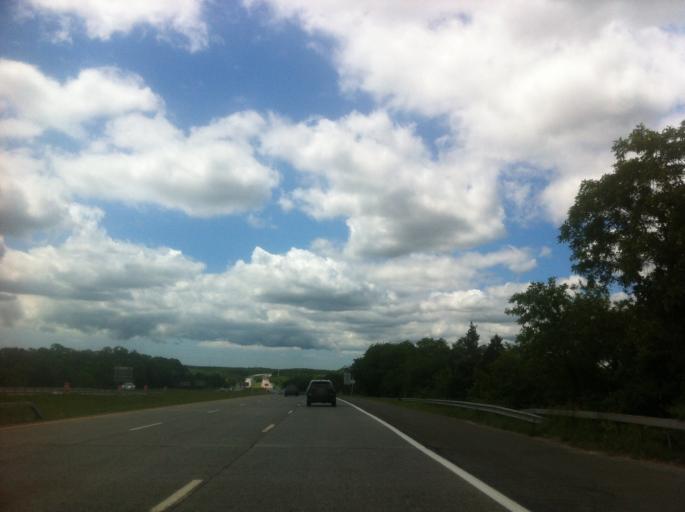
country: US
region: New York
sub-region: Suffolk County
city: Calverton
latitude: 40.9132
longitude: -72.7340
